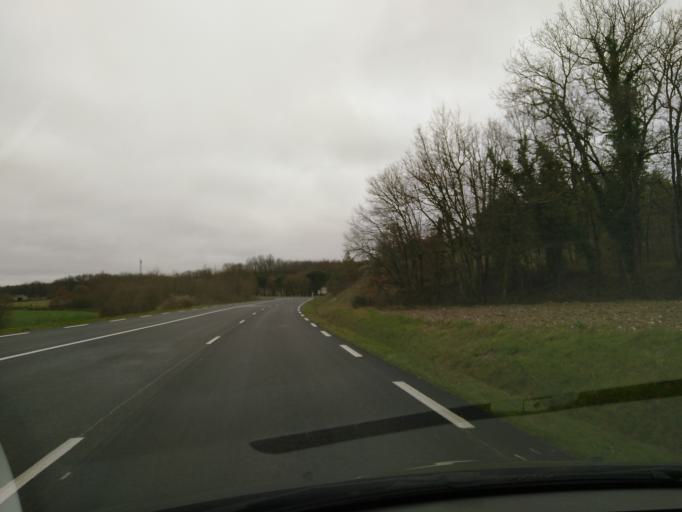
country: FR
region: Aquitaine
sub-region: Departement de la Dordogne
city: Monbazillac
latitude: 44.7280
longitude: 0.5487
